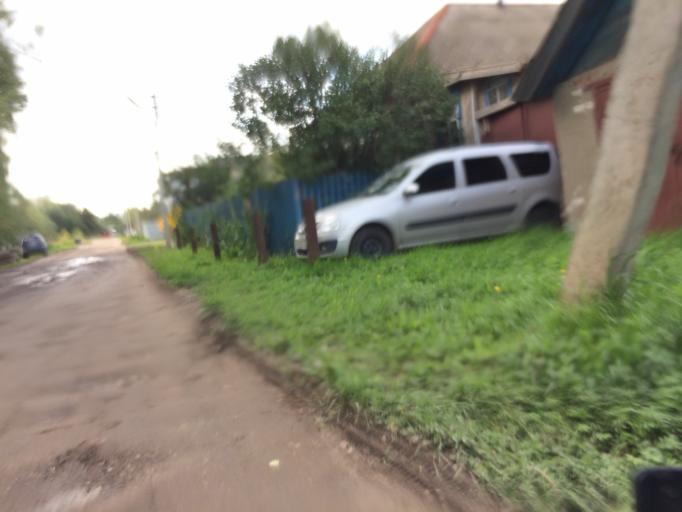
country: RU
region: Mariy-El
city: Yoshkar-Ola
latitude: 56.6542
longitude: 48.0126
